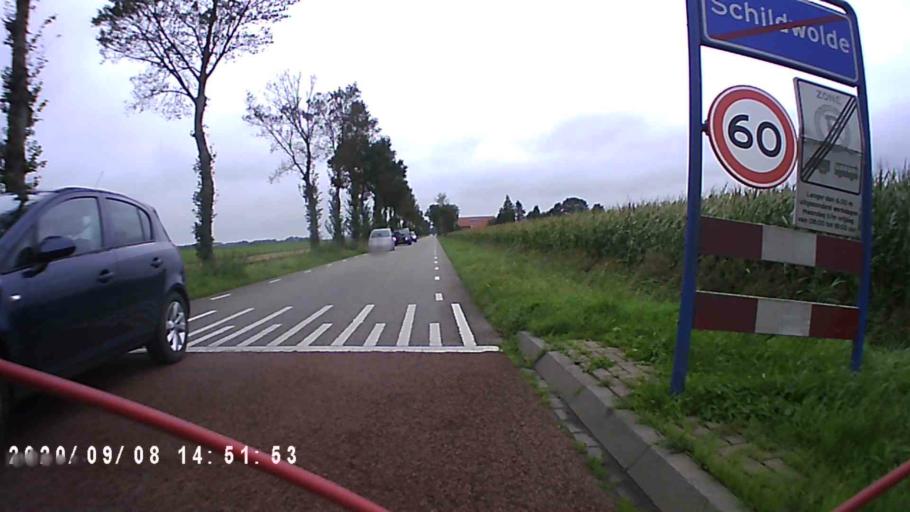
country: NL
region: Groningen
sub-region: Gemeente Slochteren
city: Slochteren
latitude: 53.2468
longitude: 6.7965
